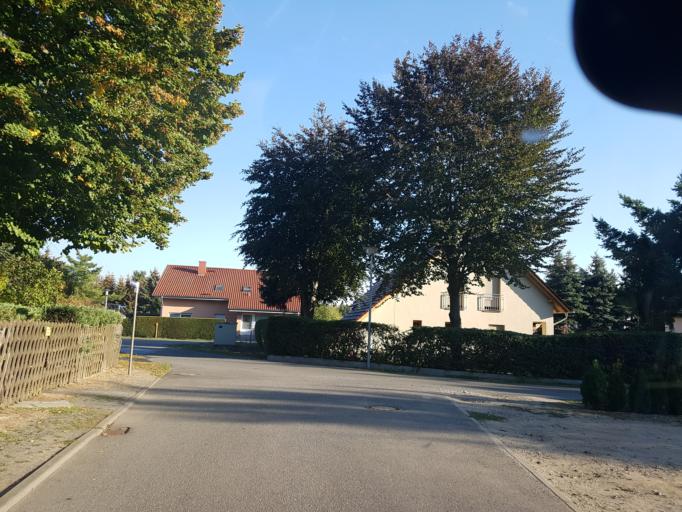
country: DE
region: Brandenburg
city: Bad Liebenwerda
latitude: 51.5203
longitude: 13.4182
